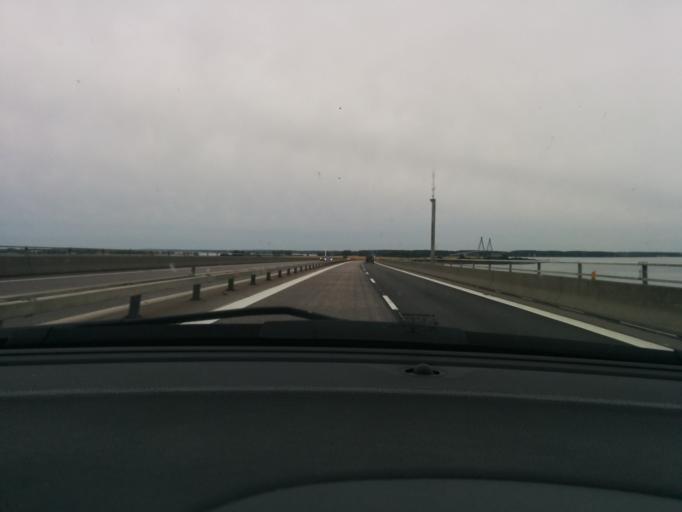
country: DK
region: Zealand
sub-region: Vordingborg Kommune
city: Nyrad
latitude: 54.9653
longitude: 11.9998
